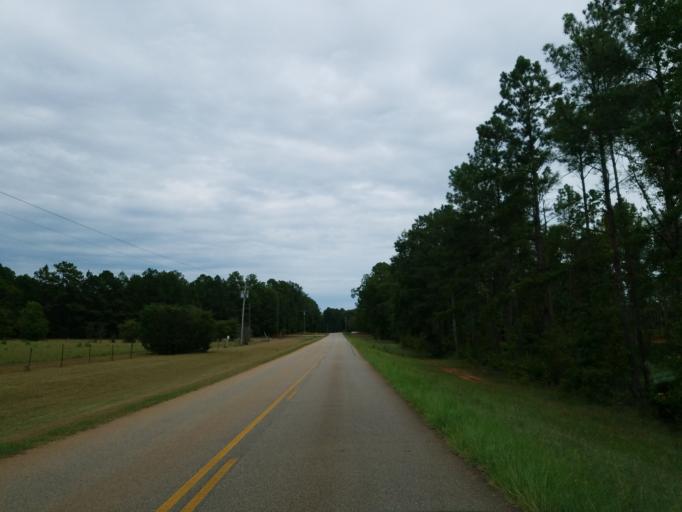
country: US
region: Georgia
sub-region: Monroe County
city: Forsyth
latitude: 32.9777
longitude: -84.0032
